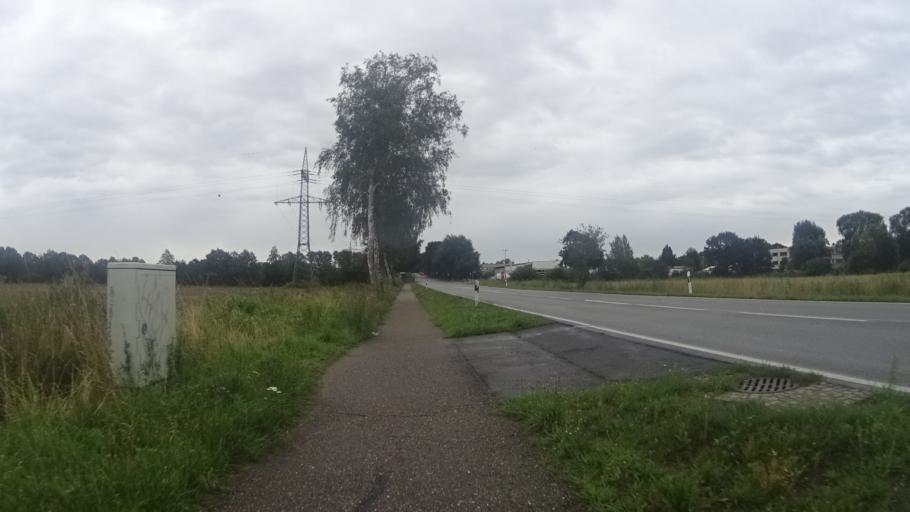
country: DE
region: Schleswig-Holstein
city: Elmshorn
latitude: 53.7801
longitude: 9.6453
